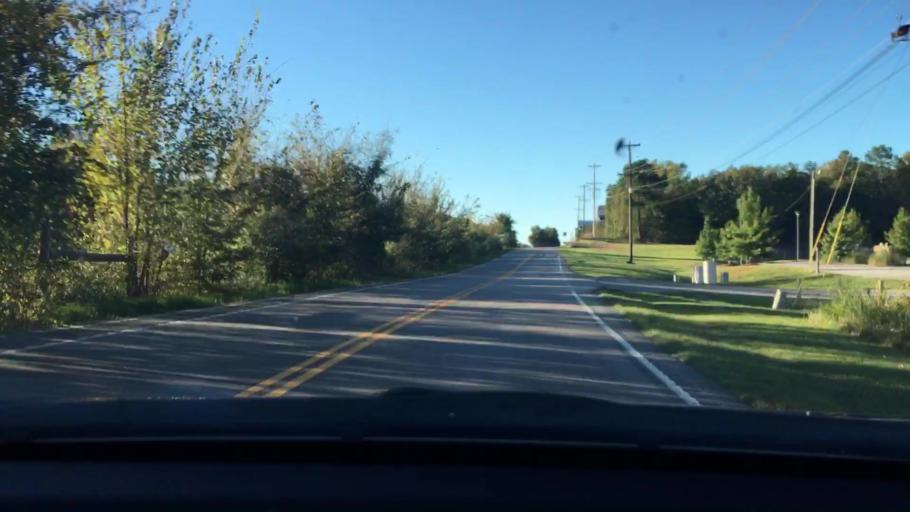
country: US
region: South Carolina
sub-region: Lexington County
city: Irmo
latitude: 34.1029
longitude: -81.1784
